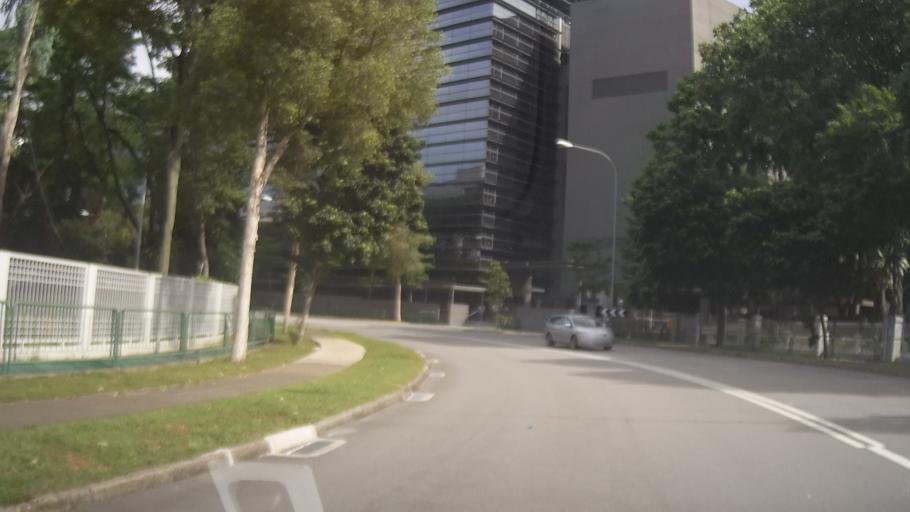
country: SG
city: Singapore
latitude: 1.3265
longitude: 103.8724
